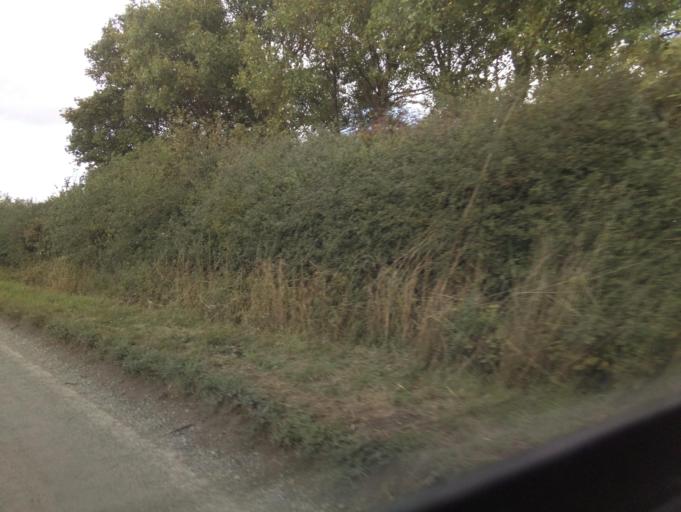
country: GB
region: England
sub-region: North Yorkshire
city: Bedale
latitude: 54.2323
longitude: -1.6677
